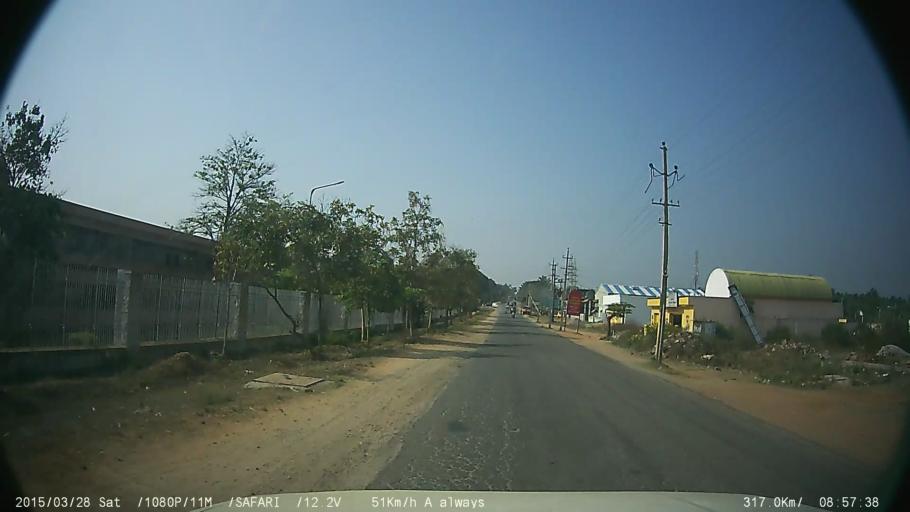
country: IN
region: Karnataka
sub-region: Mysore
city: Mysore
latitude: 12.3594
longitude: 76.5810
